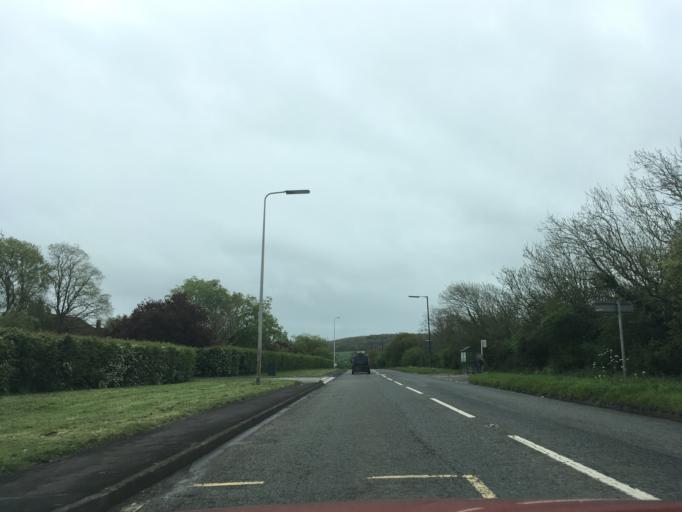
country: GB
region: England
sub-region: North Somerset
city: St. Georges
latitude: 51.3326
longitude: -2.9007
